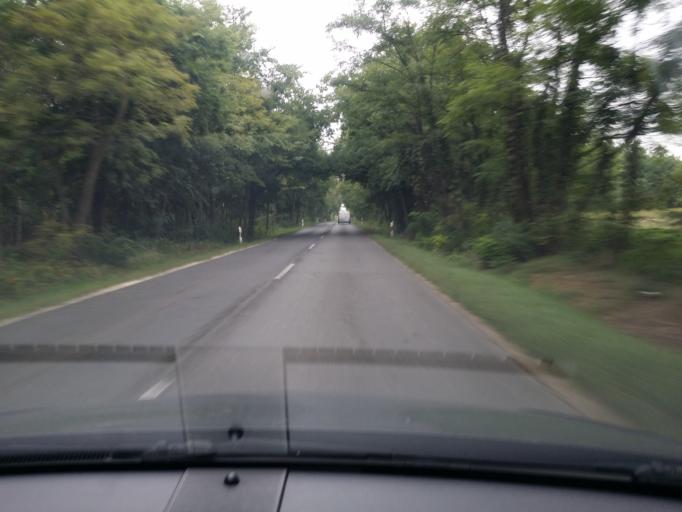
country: HU
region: Pest
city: Dunaharaszti
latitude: 47.3402
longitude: 19.1279
